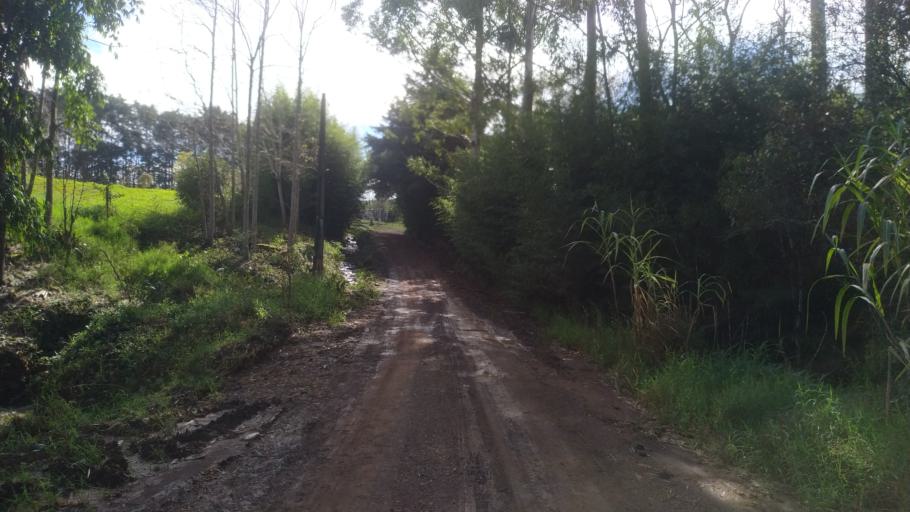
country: BR
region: Santa Catarina
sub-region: Chapeco
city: Chapeco
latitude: -27.1563
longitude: -52.5964
